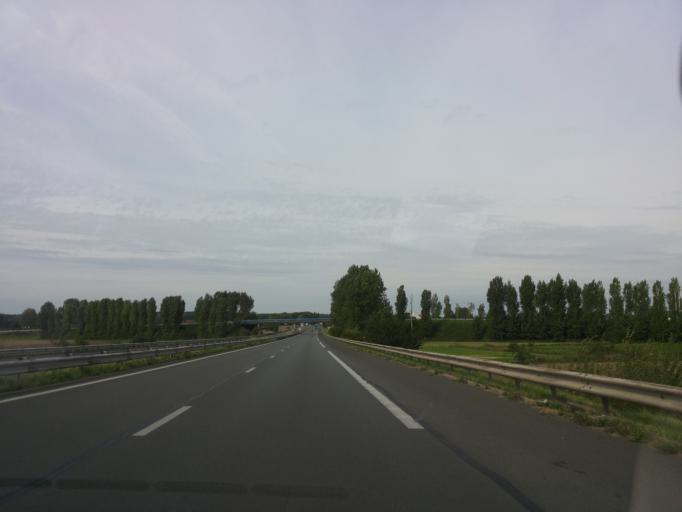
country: FR
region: Nord-Pas-de-Calais
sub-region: Departement du Pas-de-Calais
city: Labeuvriere
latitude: 50.5203
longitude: 2.5778
